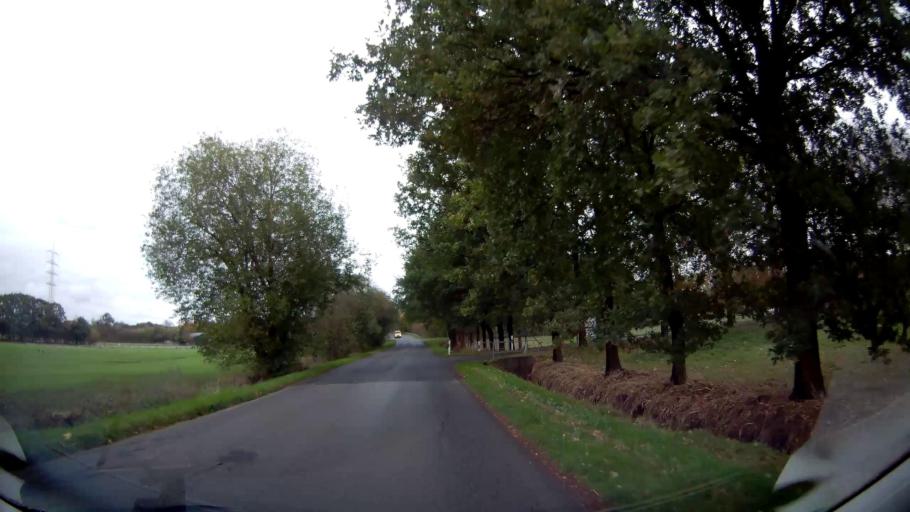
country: DE
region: North Rhine-Westphalia
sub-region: Regierungsbezirk Munster
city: Gladbeck
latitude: 51.6010
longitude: 6.9359
